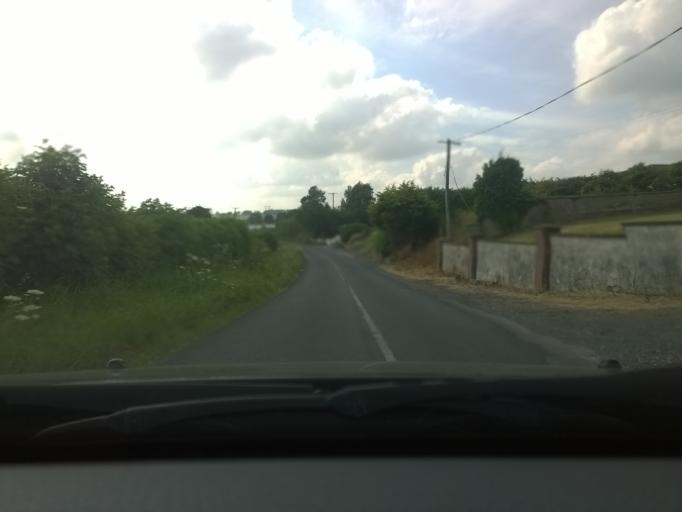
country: IE
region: Leinster
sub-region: Kildare
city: Kildare
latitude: 53.1771
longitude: -6.9207
